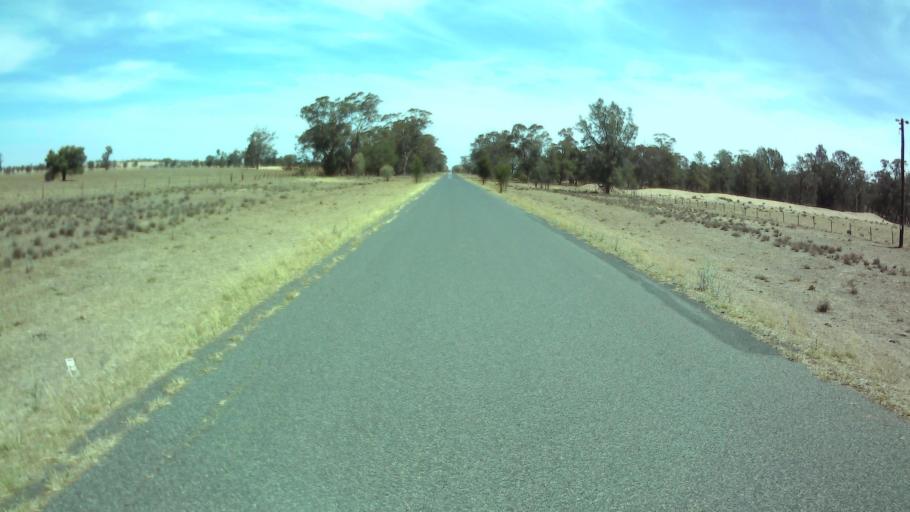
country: AU
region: New South Wales
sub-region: Weddin
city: Grenfell
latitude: -33.8627
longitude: 147.7462
